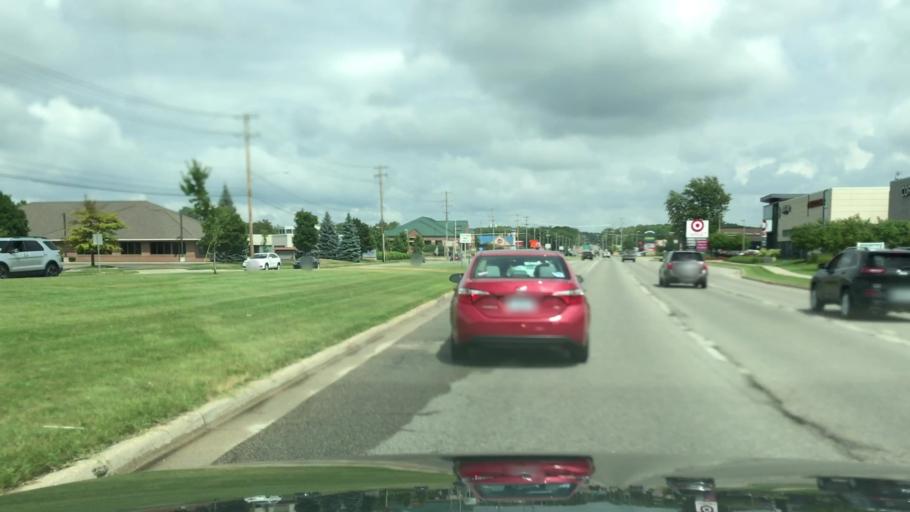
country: US
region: Michigan
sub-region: Kent County
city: Grandville
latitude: 42.8845
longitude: -85.7430
